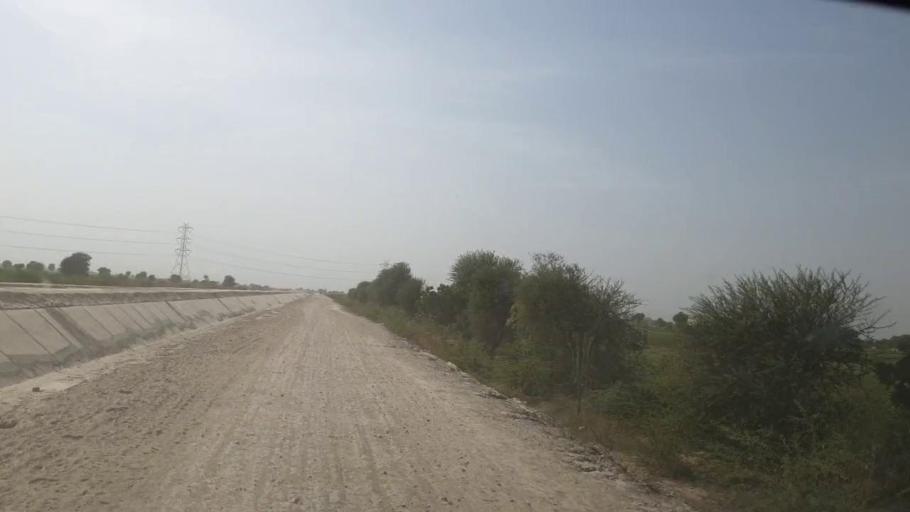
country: PK
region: Sindh
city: Nabisar
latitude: 25.0582
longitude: 69.5486
